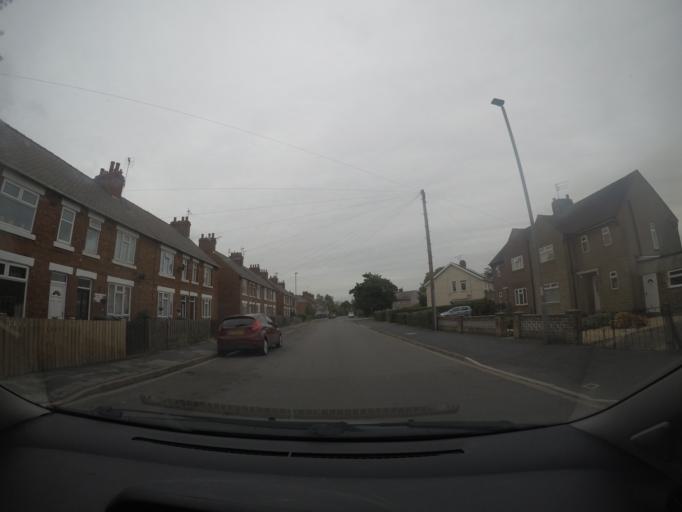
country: GB
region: England
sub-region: North Yorkshire
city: Selby
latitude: 53.7789
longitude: -1.0537
